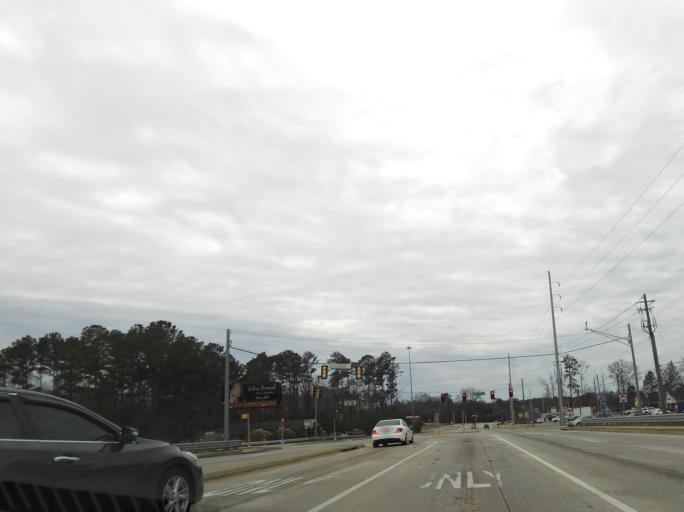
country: US
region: Georgia
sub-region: Bibb County
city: West Point
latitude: 32.8801
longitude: -83.7700
